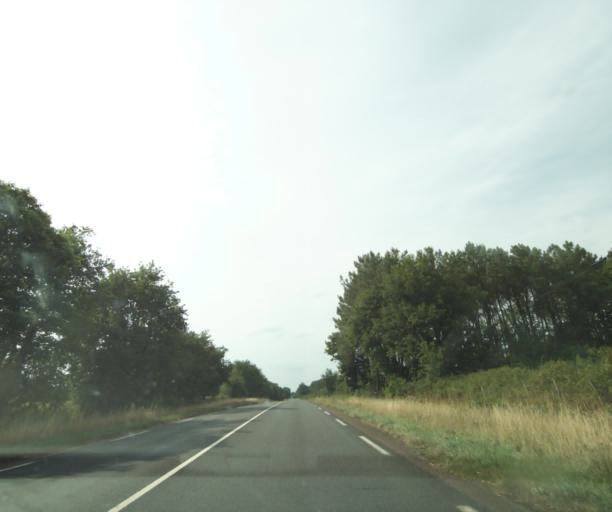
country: FR
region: Pays de la Loire
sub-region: Departement de la Sarthe
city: Marigne-Laille
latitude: 47.7955
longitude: 0.3339
